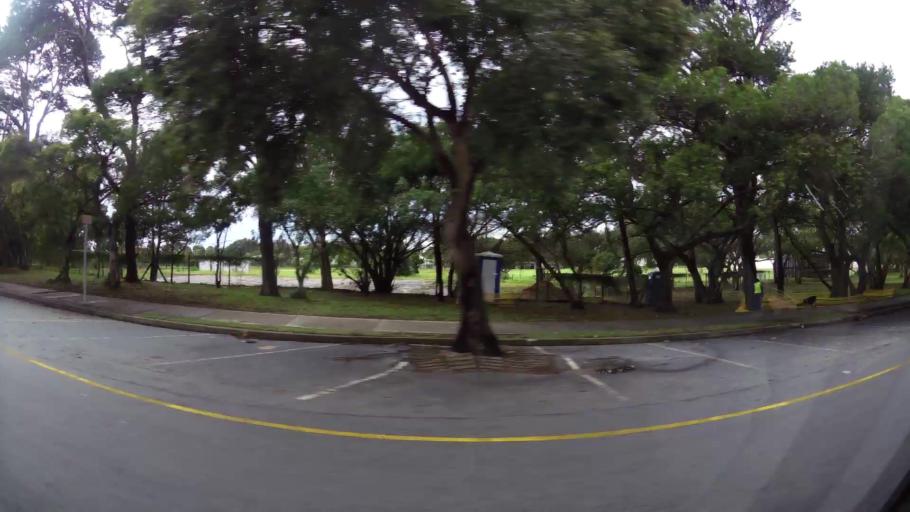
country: ZA
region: Eastern Cape
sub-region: Nelson Mandela Bay Metropolitan Municipality
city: Port Elizabeth
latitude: -33.9641
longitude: 25.6040
